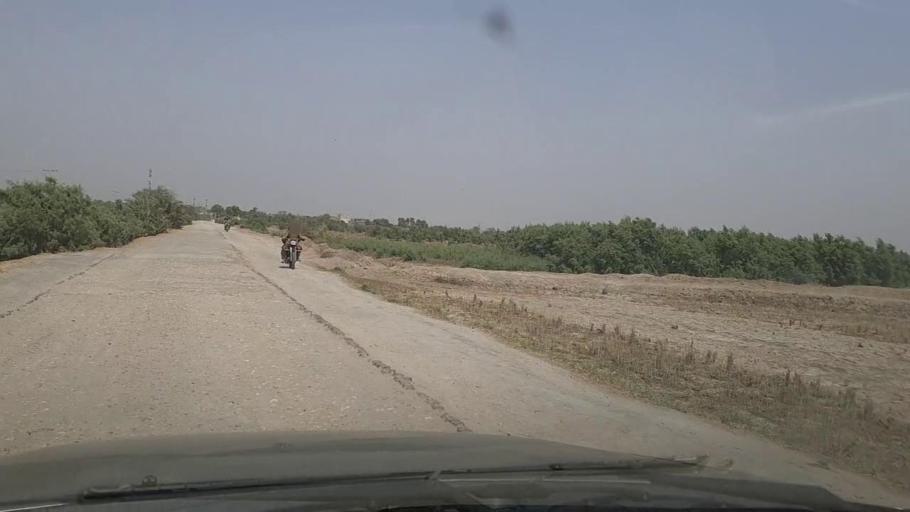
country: PK
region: Balochistan
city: Sohbatpur
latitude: 28.4220
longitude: 68.6785
